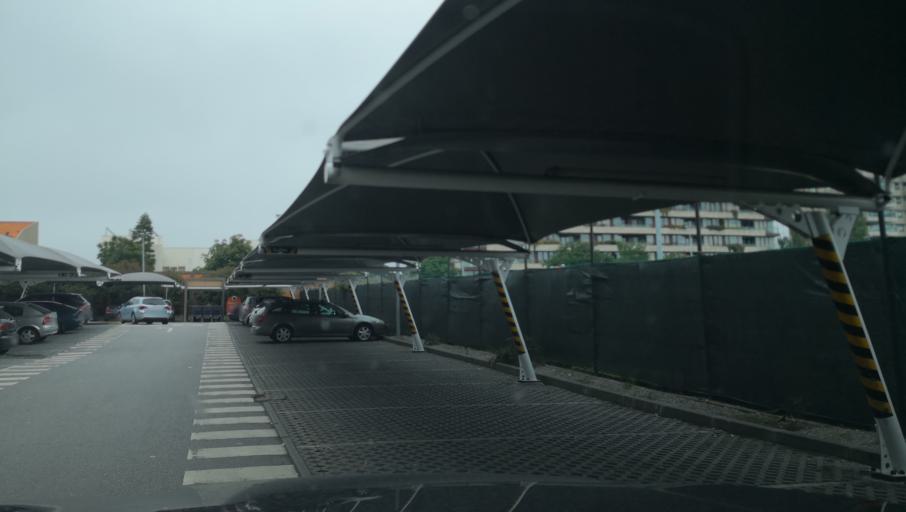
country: PT
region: Porto
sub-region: Vila Nova de Gaia
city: Canidelo
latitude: 41.1545
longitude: -8.6637
